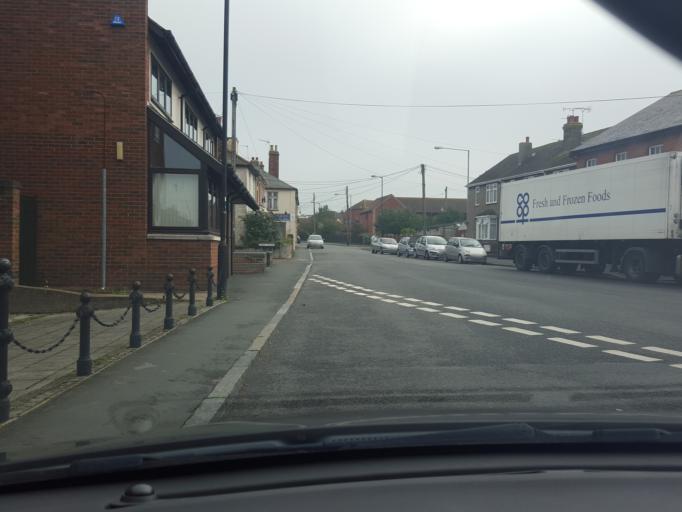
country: GB
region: England
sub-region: Essex
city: Brightlingsea
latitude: 51.8097
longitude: 1.0212
